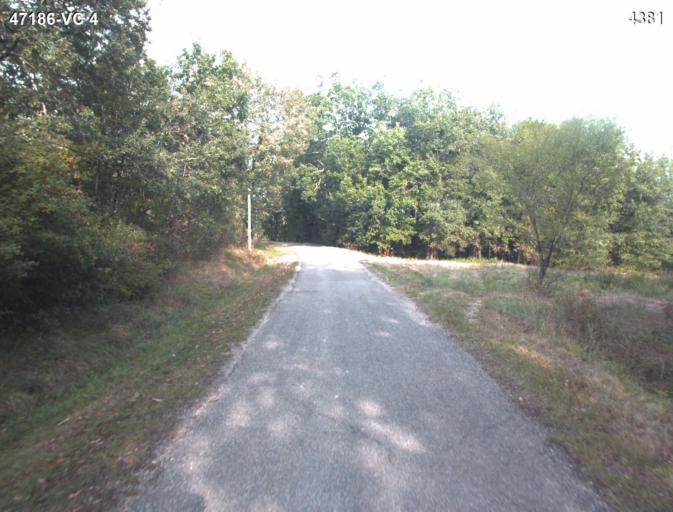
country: FR
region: Aquitaine
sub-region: Departement du Lot-et-Garonne
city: Sainte-Colombe-en-Bruilhois
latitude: 44.1945
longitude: 0.4510
